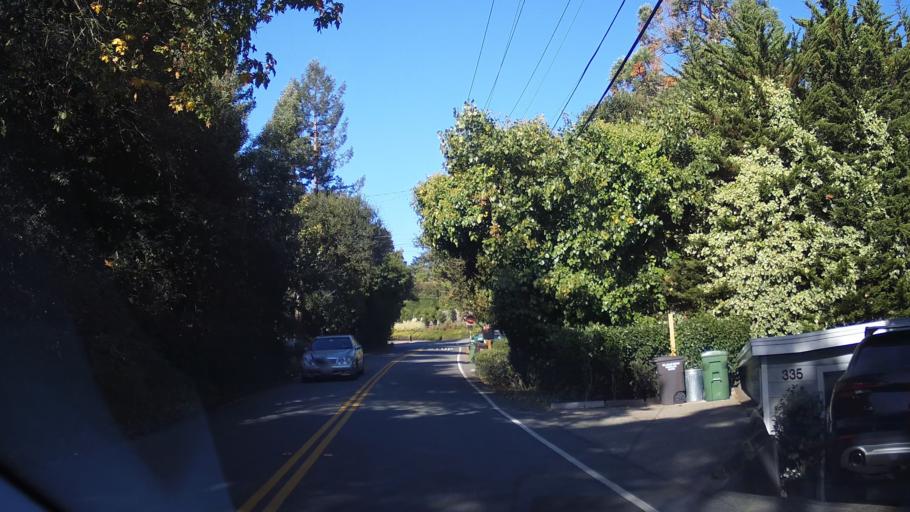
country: US
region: California
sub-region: Marin County
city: Mill Valley
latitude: 37.9000
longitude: -122.5440
